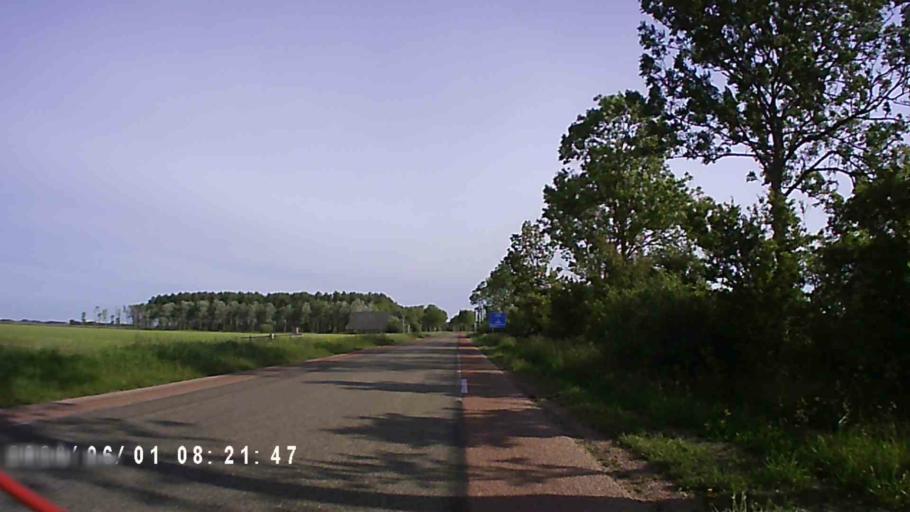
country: NL
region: Friesland
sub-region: Gemeente Ferwerderadiel
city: Burdaard
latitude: 53.3014
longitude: 5.8750
